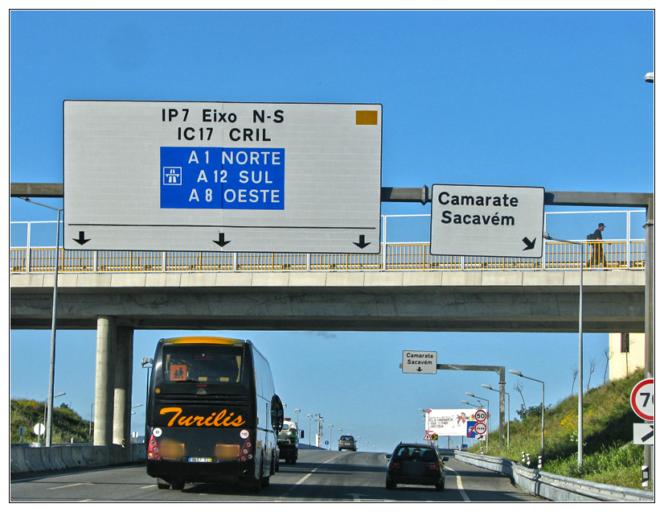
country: PT
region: Lisbon
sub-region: Loures
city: Camarate
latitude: 38.7947
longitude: -9.1431
